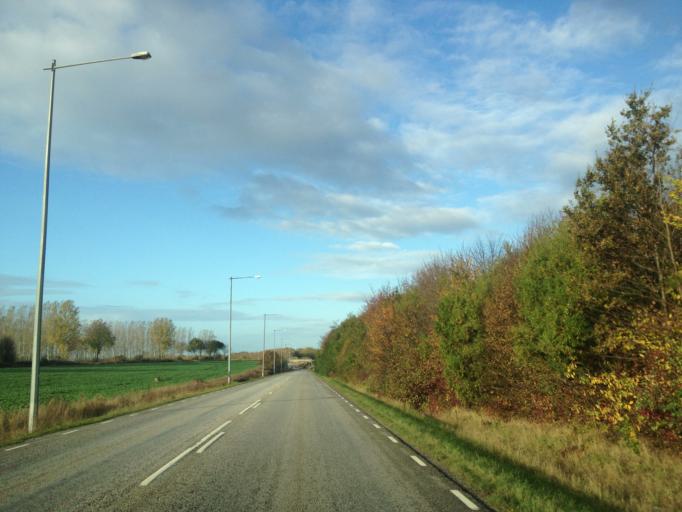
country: SE
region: Skane
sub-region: Lomma Kommun
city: Lomma
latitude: 55.6638
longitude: 13.0818
